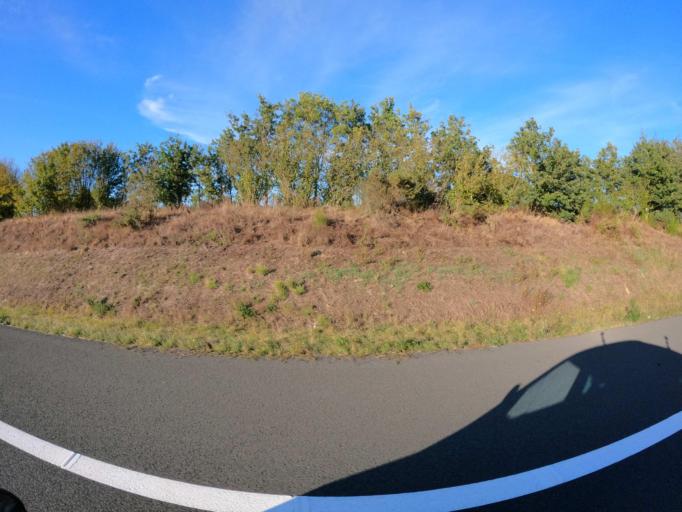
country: FR
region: Pays de la Loire
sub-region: Departement de Maine-et-Loire
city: Saint-Lambert-du-Lattay
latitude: 47.2431
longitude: -0.6627
